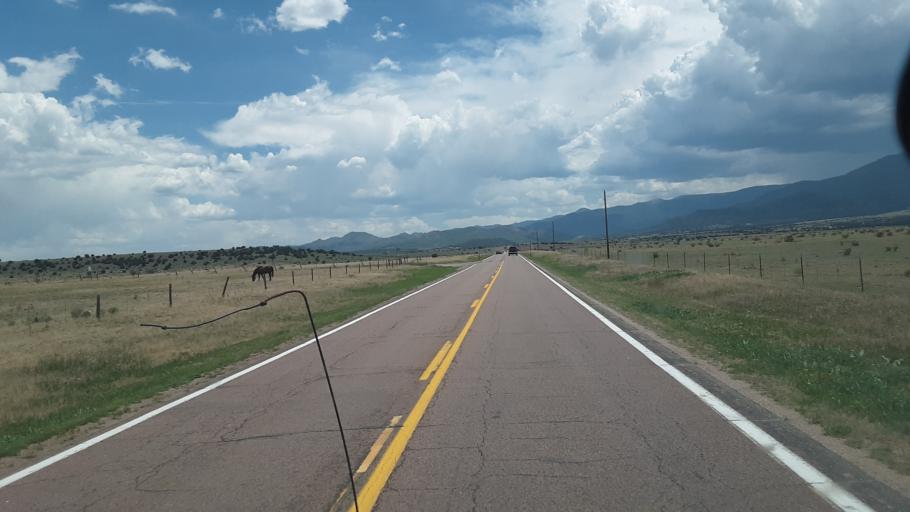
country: US
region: Colorado
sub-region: Fremont County
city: Florence
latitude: 38.2882
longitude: -105.0875
